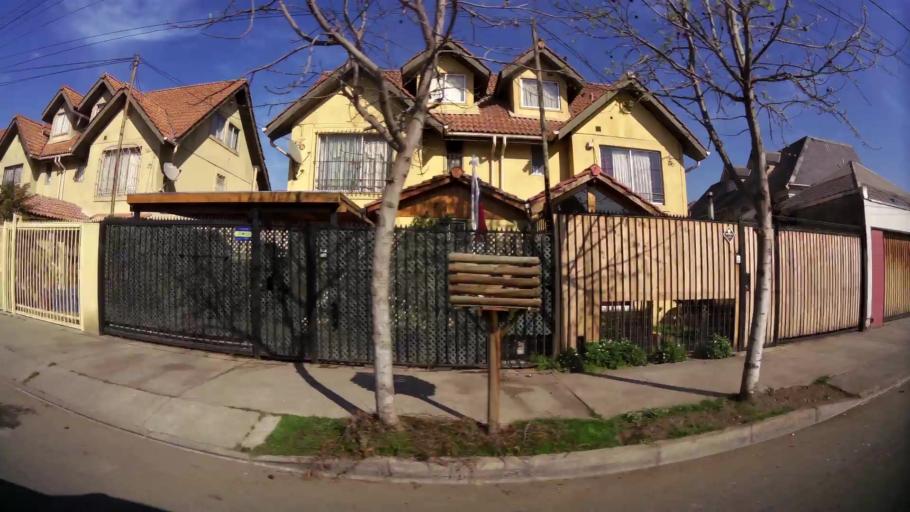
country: CL
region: Santiago Metropolitan
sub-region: Provincia de Santiago
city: Lo Prado
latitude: -33.4500
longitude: -70.7632
